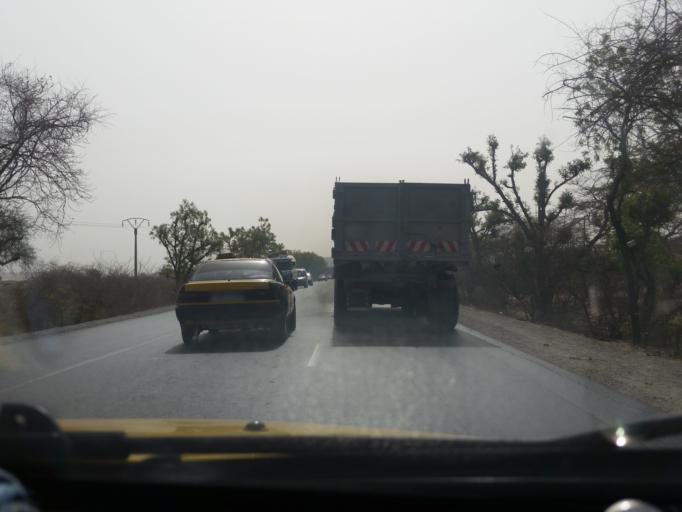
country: SN
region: Thies
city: Thies Nones
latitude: 14.7651
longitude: -17.0117
